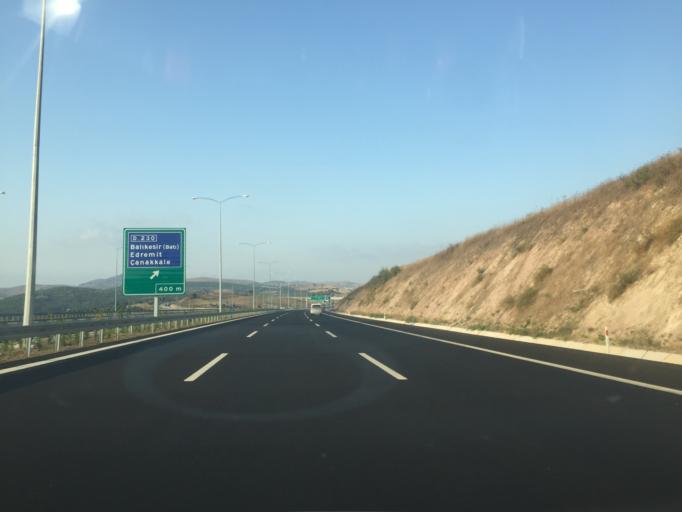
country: TR
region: Balikesir
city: Ertugrul
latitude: 39.6311
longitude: 27.7080
